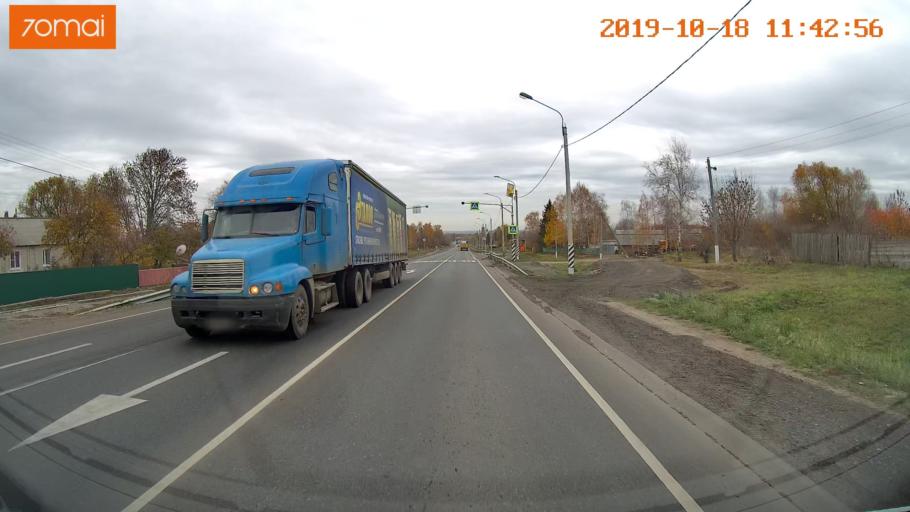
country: RU
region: Rjazan
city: Oktyabr'skiy
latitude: 54.1928
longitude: 38.9364
